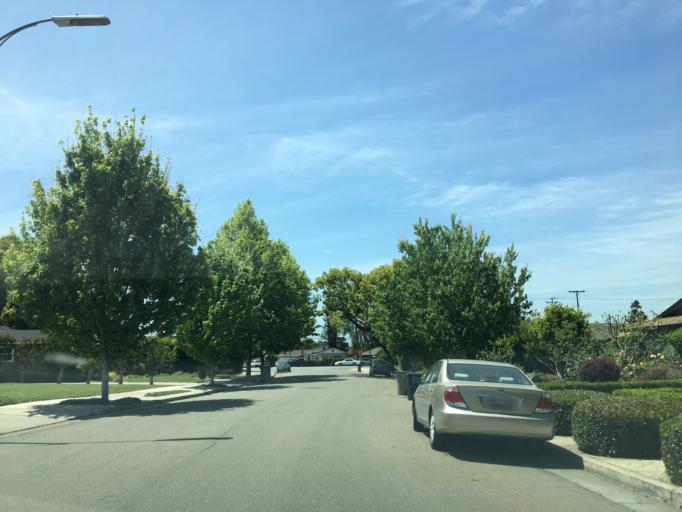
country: US
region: California
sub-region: Santa Clara County
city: Buena Vista
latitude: 37.2985
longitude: -121.9122
